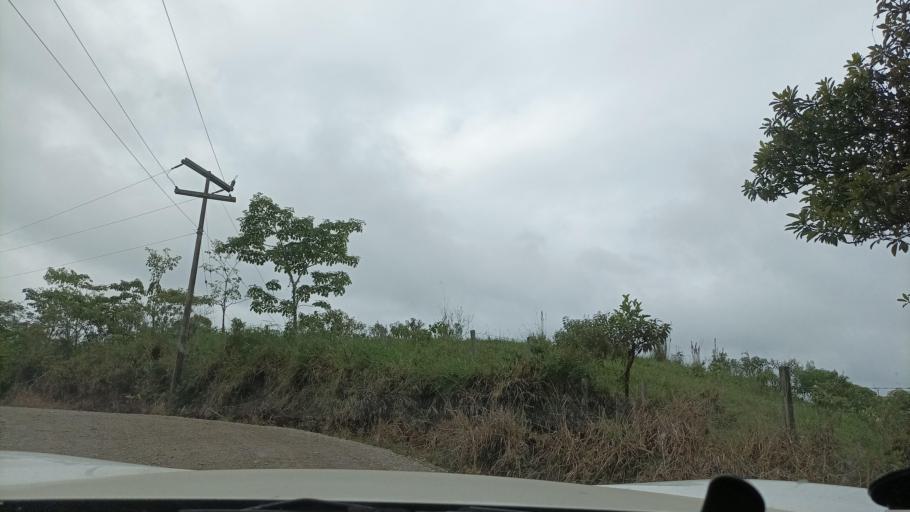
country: MX
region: Veracruz
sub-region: Uxpanapa
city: Poblado 10
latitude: 17.4237
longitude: -94.4185
